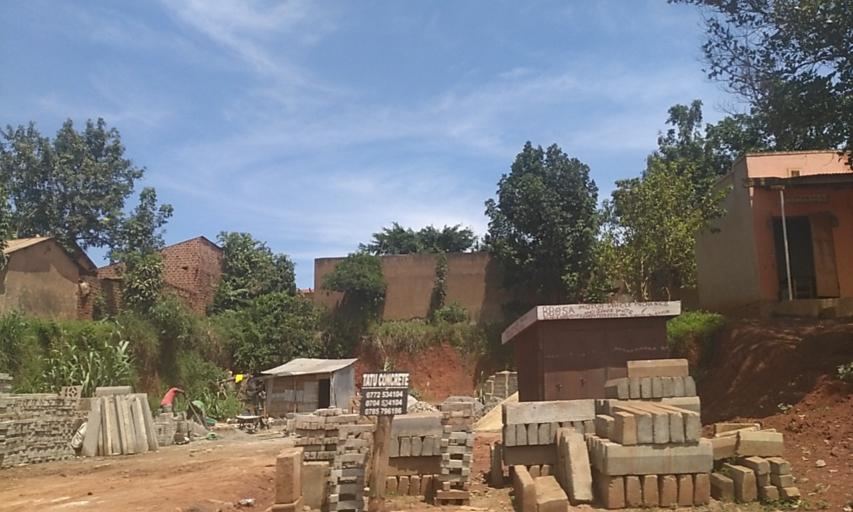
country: UG
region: Central Region
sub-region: Wakiso District
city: Wakiso
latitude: 0.4032
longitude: 32.4755
